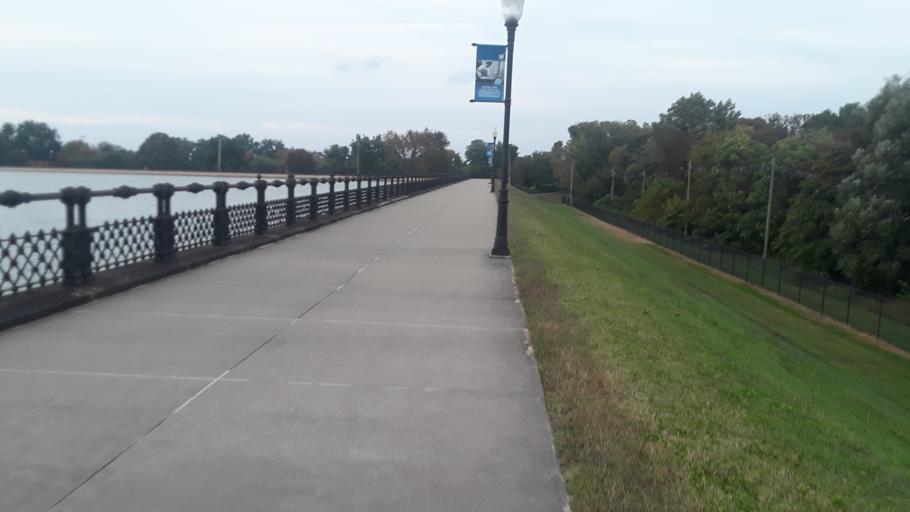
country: US
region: Kentucky
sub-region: Jefferson County
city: Indian Hills
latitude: 38.2569
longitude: -85.6780
